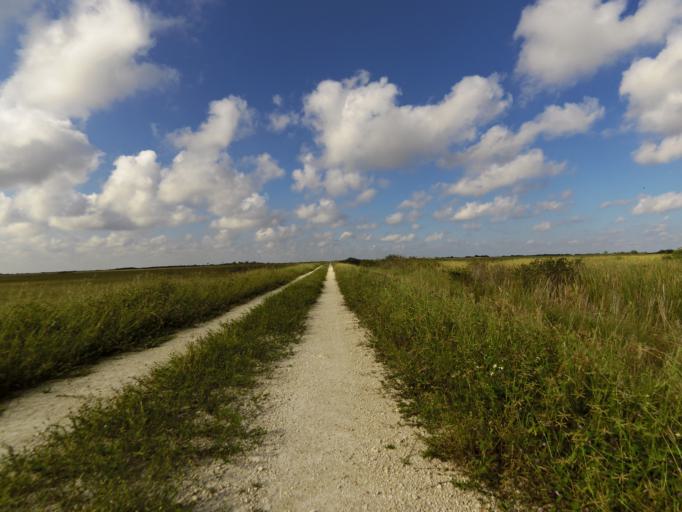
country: US
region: Florida
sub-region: Broward County
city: Weston
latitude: 26.0591
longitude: -80.4493
